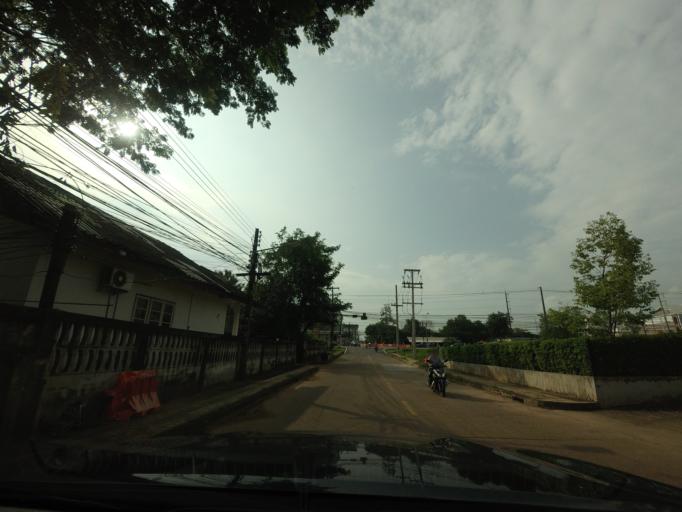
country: TH
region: Nong Khai
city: Nong Khai
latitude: 17.8791
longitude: 102.7464
